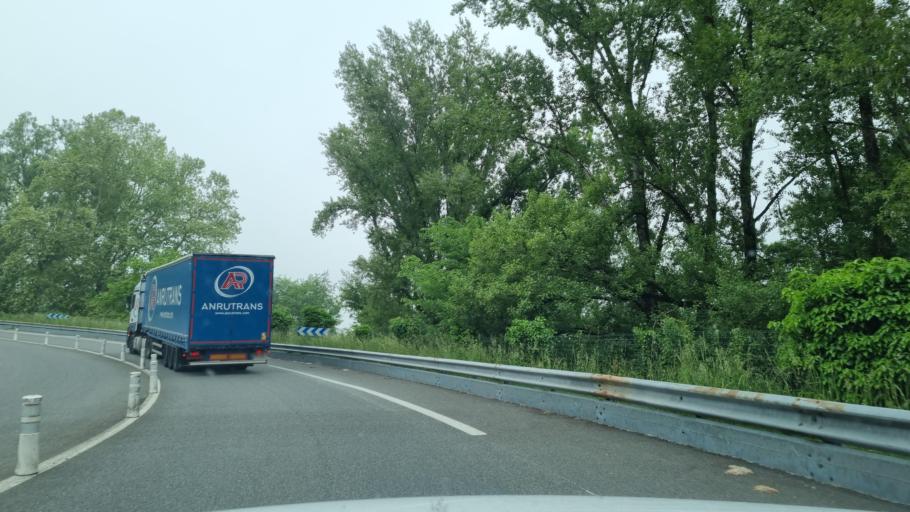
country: FR
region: Aquitaine
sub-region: Departement des Pyrenees-Atlantiques
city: Orthez
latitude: 43.4701
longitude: -0.7458
